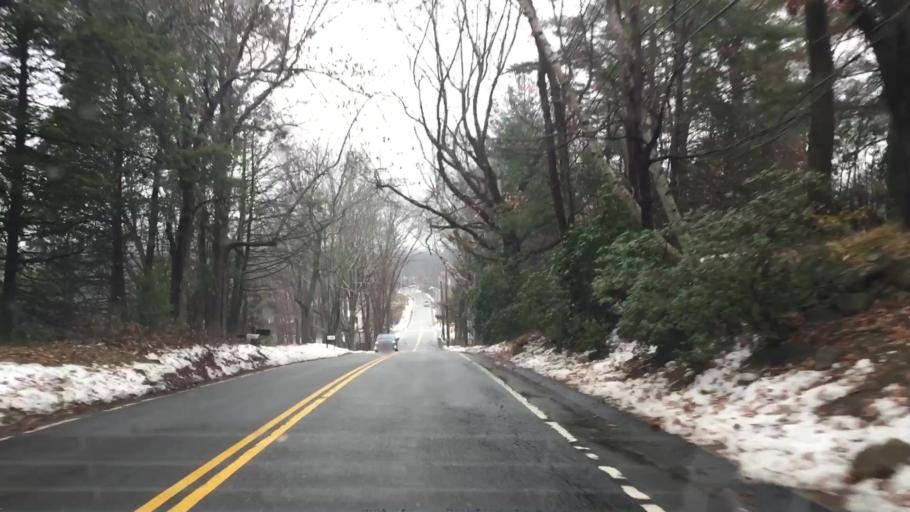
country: US
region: Massachusetts
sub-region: Essex County
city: North Andover
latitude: 42.6909
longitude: -71.0940
